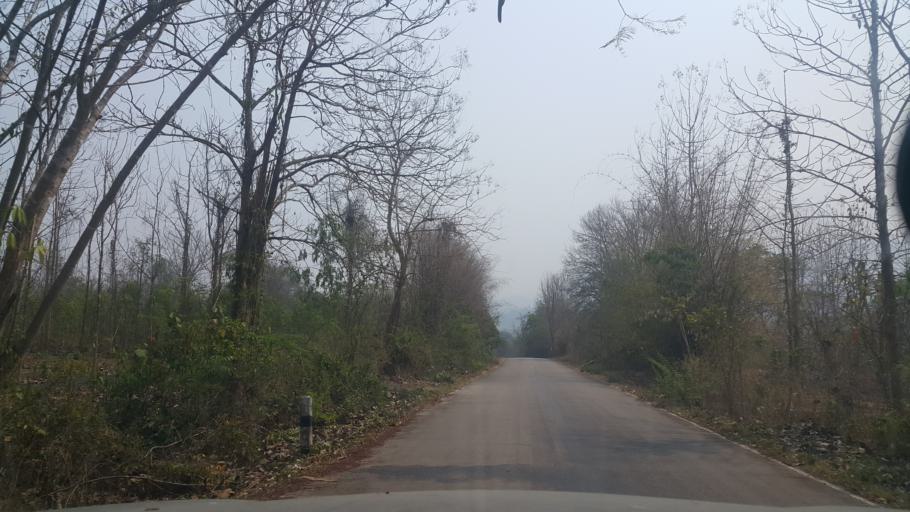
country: TH
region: Lampang
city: Sop Prap
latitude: 17.7949
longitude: 99.2585
